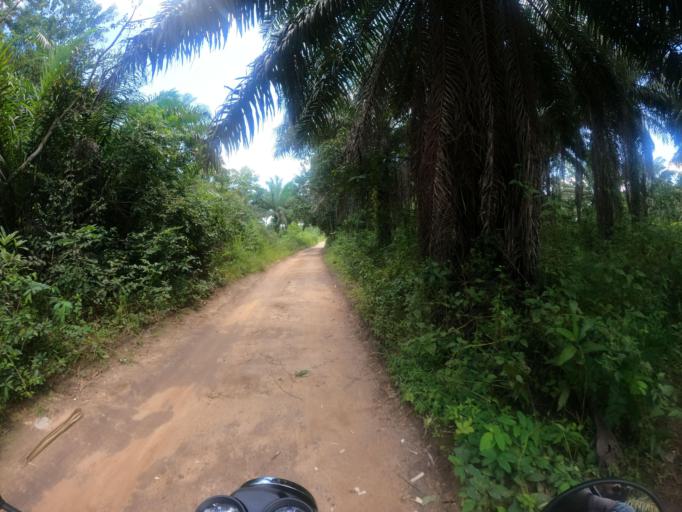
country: SL
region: Northern Province
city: Makeni
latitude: 8.8567
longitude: -12.1126
